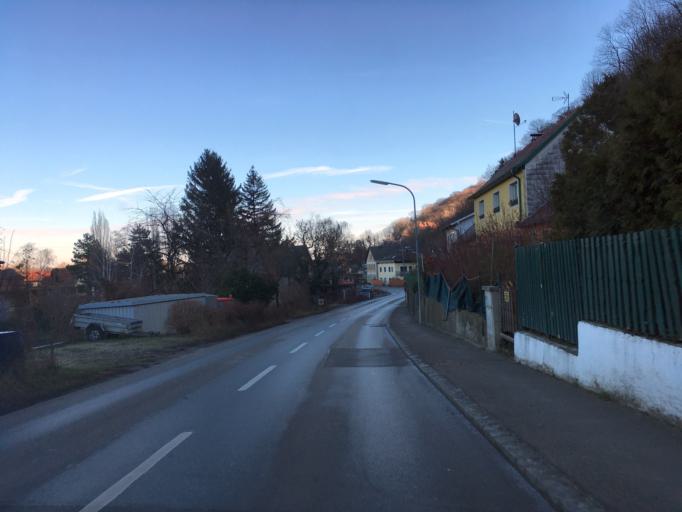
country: AT
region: Lower Austria
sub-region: Politischer Bezirk Korneuburg
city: Spillern
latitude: 48.3498
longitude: 16.2671
